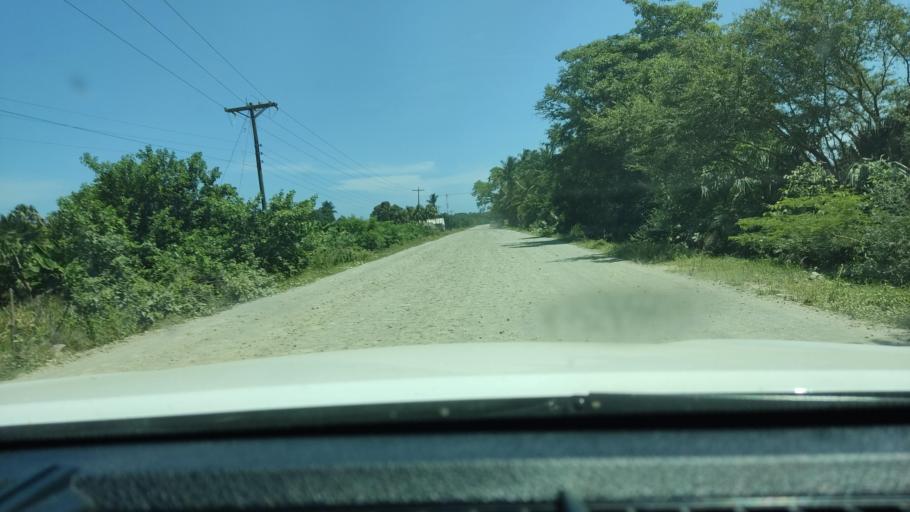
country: SV
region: Ahuachapan
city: San Francisco Menendez
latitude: 13.7625
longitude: -90.1168
